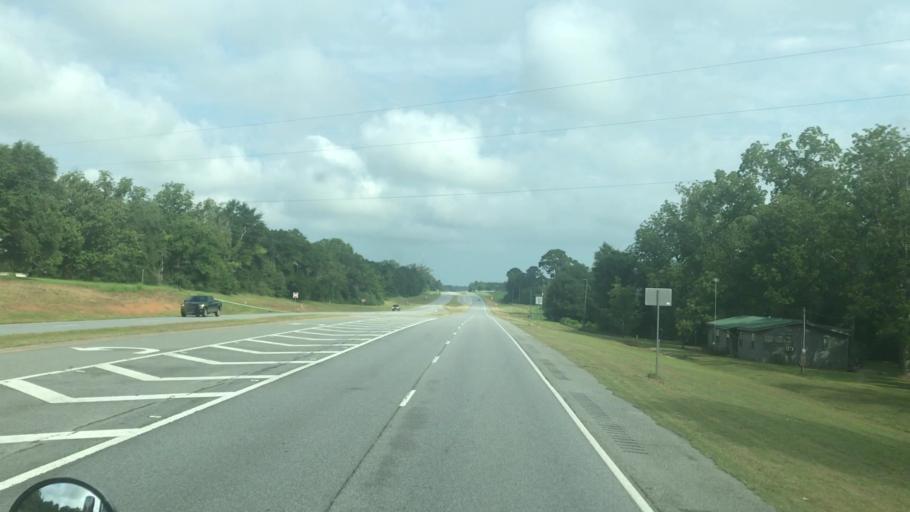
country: US
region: Georgia
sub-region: Miller County
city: Colquitt
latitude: 31.2496
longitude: -84.7971
